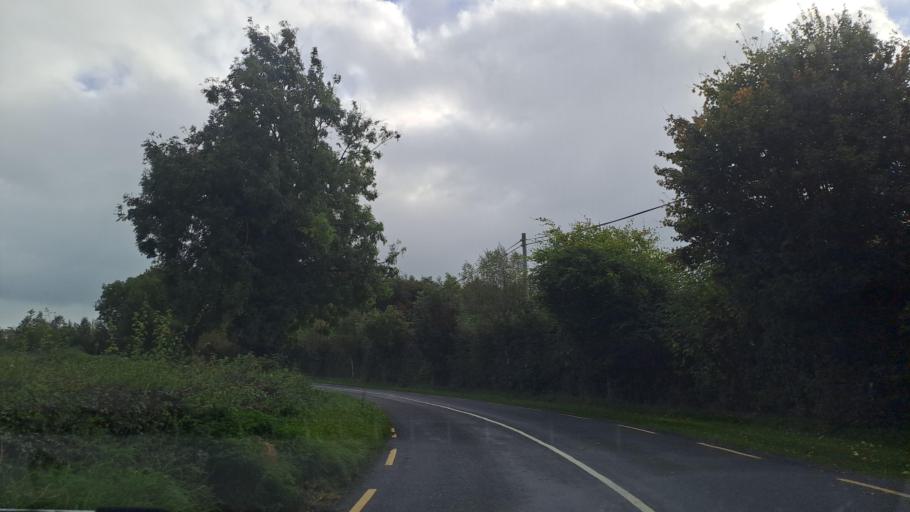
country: IE
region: Ulster
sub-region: County Monaghan
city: Carrickmacross
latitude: 53.9902
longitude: -6.7216
